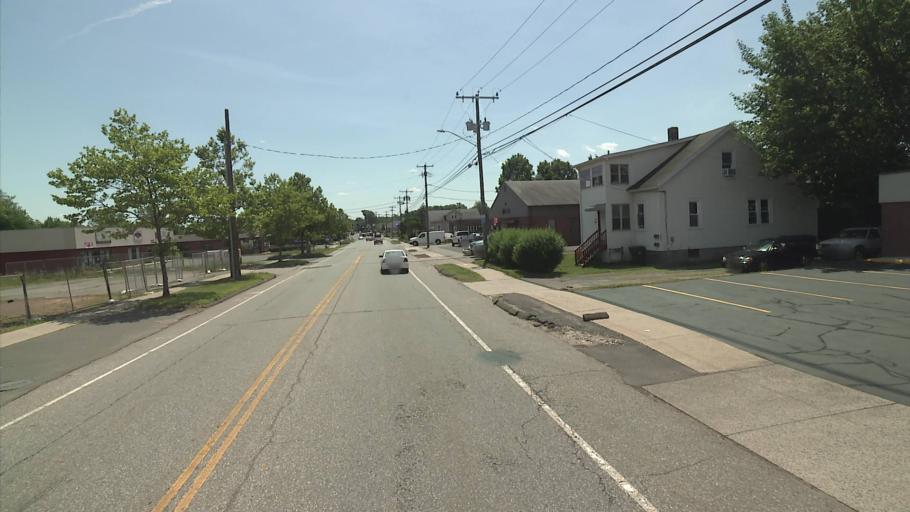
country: US
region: Connecticut
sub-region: Hartford County
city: Kensington
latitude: 41.6306
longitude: -72.7598
